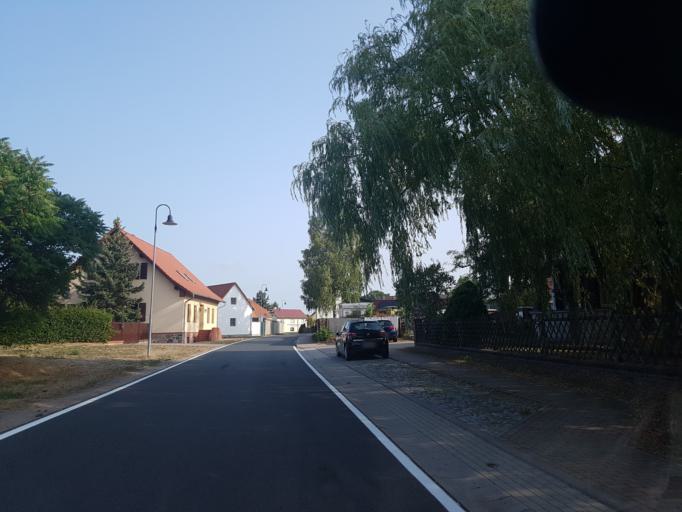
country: DE
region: Brandenburg
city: Wiesenburg
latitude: 52.0564
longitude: 12.3813
